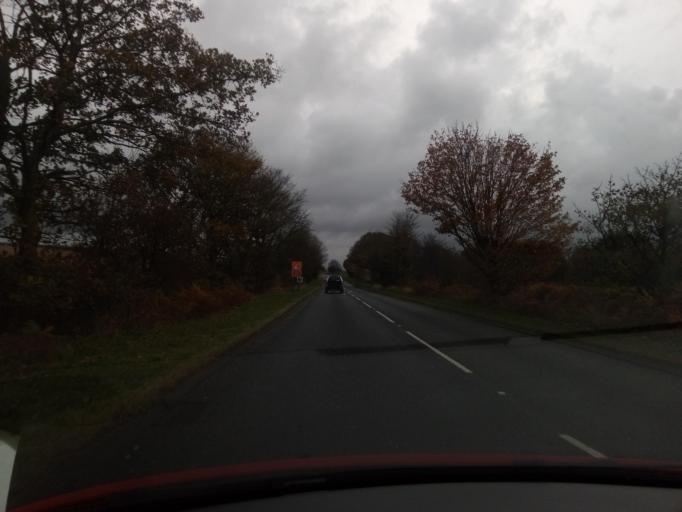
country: GB
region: England
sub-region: County Durham
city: Hamsterley
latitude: 54.6895
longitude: -1.7864
